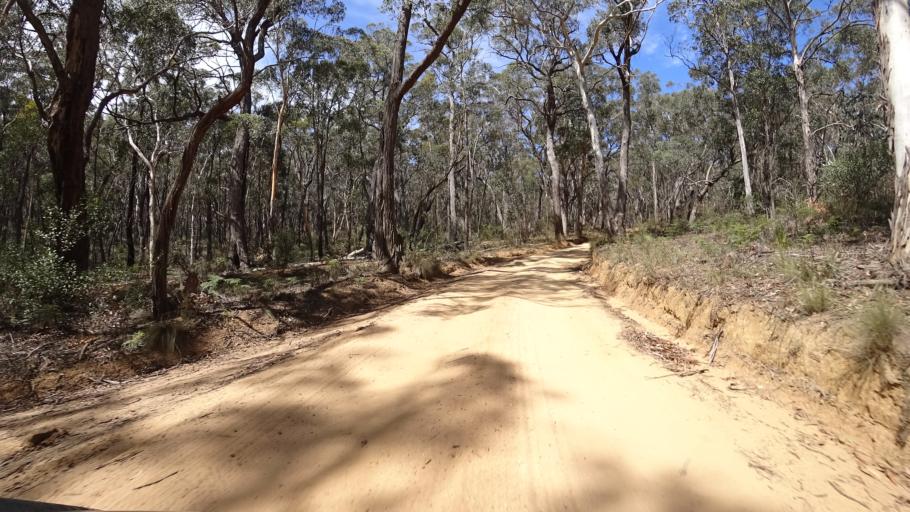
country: AU
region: New South Wales
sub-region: Lithgow
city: Lithgow
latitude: -33.2689
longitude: 150.2266
